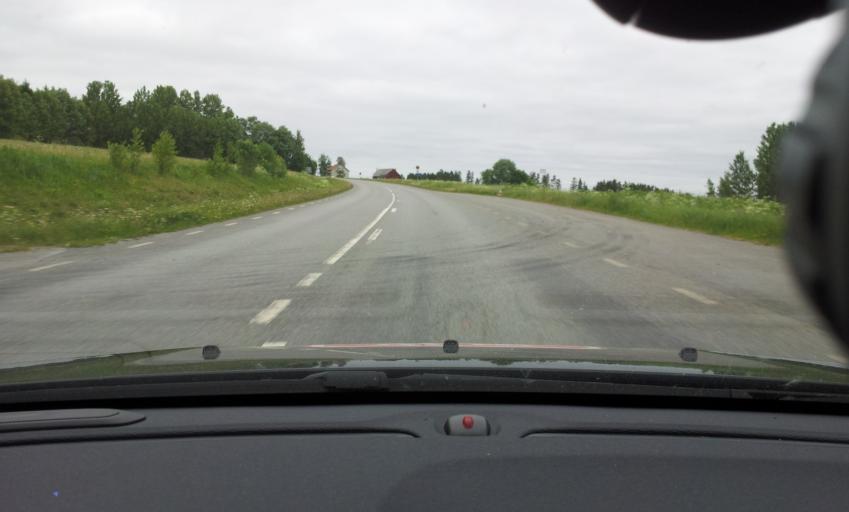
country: SE
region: Jaemtland
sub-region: Krokoms Kommun
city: Krokom
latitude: 63.1254
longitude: 14.2930
